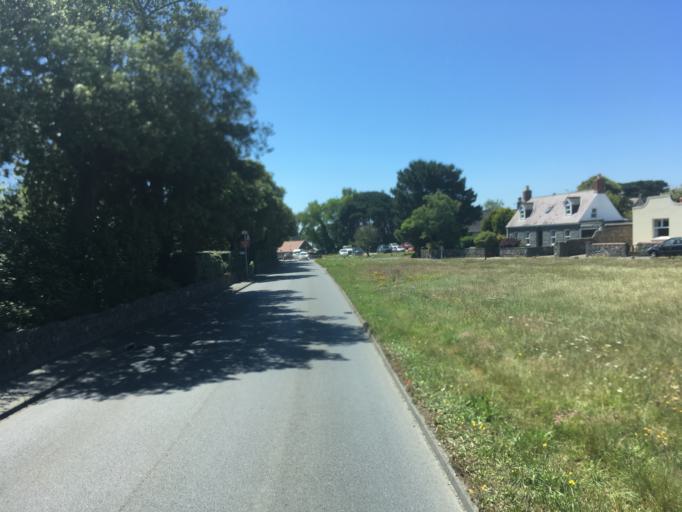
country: GG
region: St Peter Port
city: Saint Peter Port
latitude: 49.4941
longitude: -2.5371
